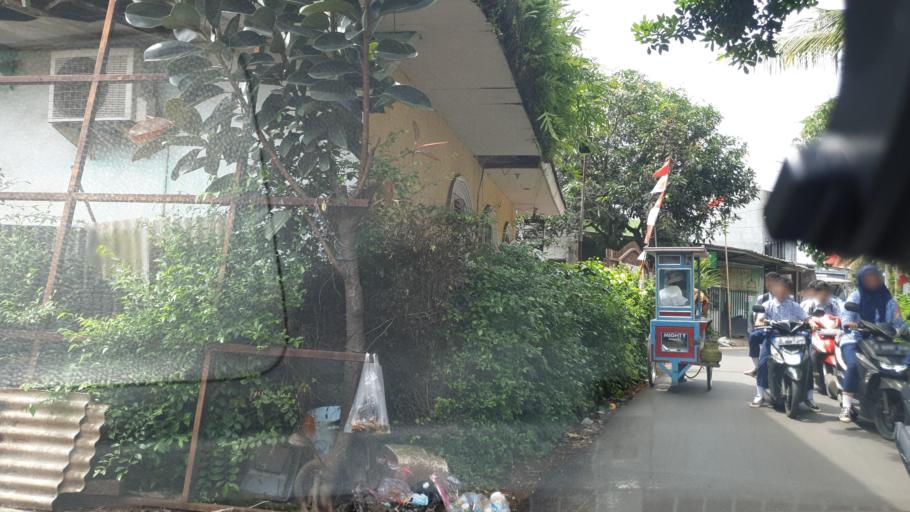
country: ID
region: West Java
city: Sawangan
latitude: -6.3712
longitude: 106.7624
